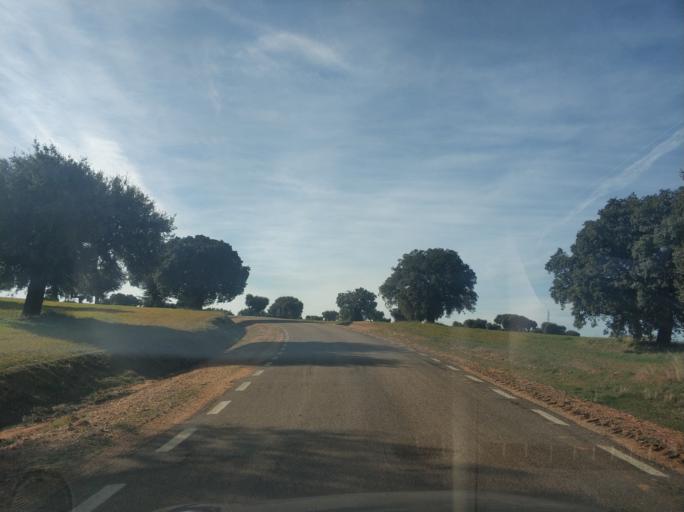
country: ES
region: Castille and Leon
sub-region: Provincia de Salamanca
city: Parada de Arriba
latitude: 41.0008
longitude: -5.8132
